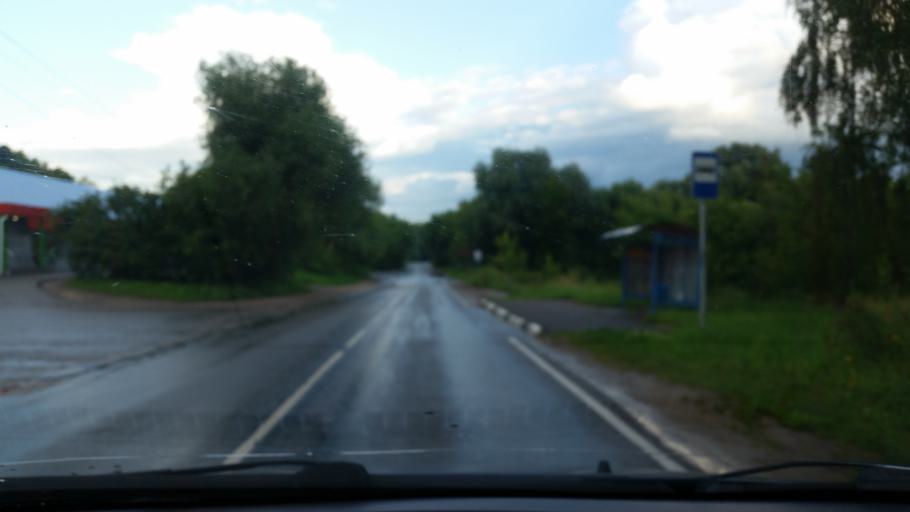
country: RU
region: Moskovskaya
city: Bol'shoye Gryzlovo
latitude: 54.8776
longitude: 37.8197
